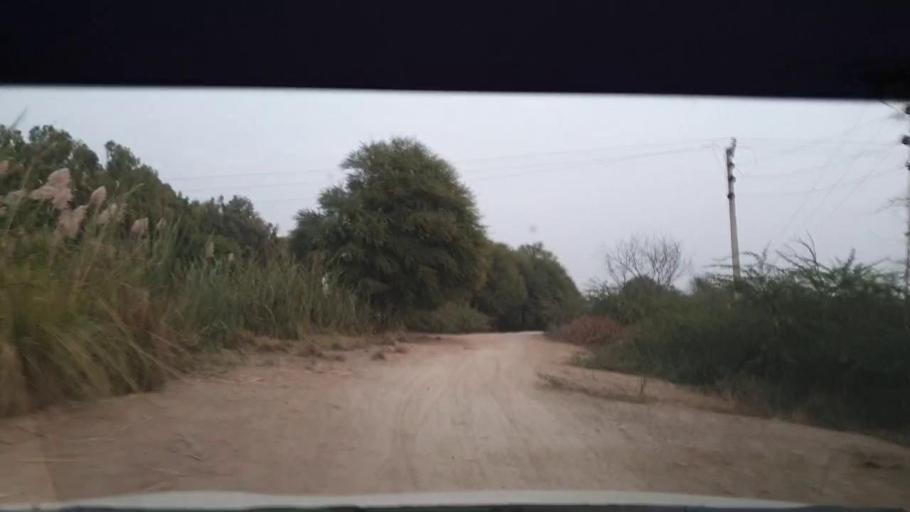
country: PK
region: Sindh
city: Berani
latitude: 25.8448
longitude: 68.7883
